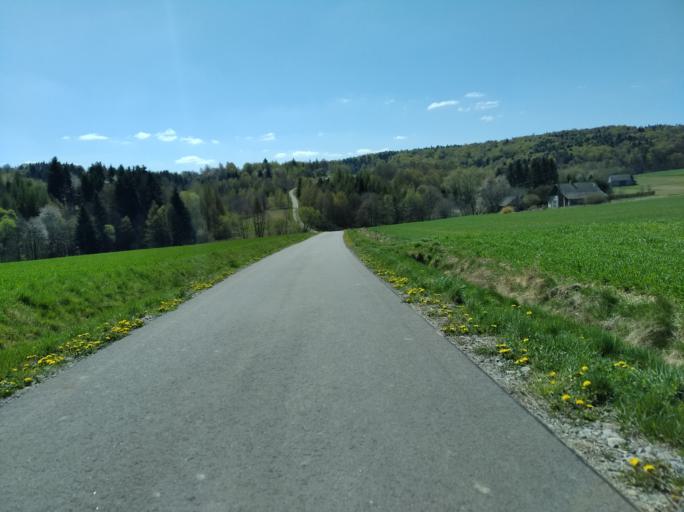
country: PL
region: Subcarpathian Voivodeship
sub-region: Powiat strzyzowski
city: Wisniowa
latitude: 49.9040
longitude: 21.6864
